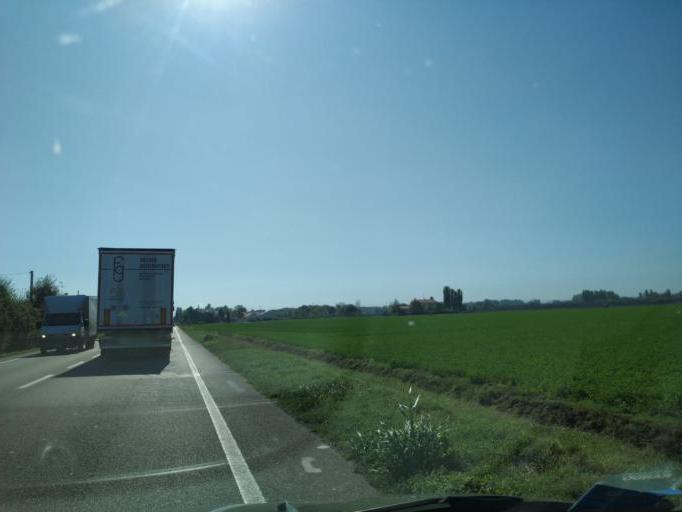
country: IT
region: Emilia-Romagna
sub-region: Provincia di Bologna
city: San Giovanni in Persiceto
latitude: 44.6481
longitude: 11.1623
